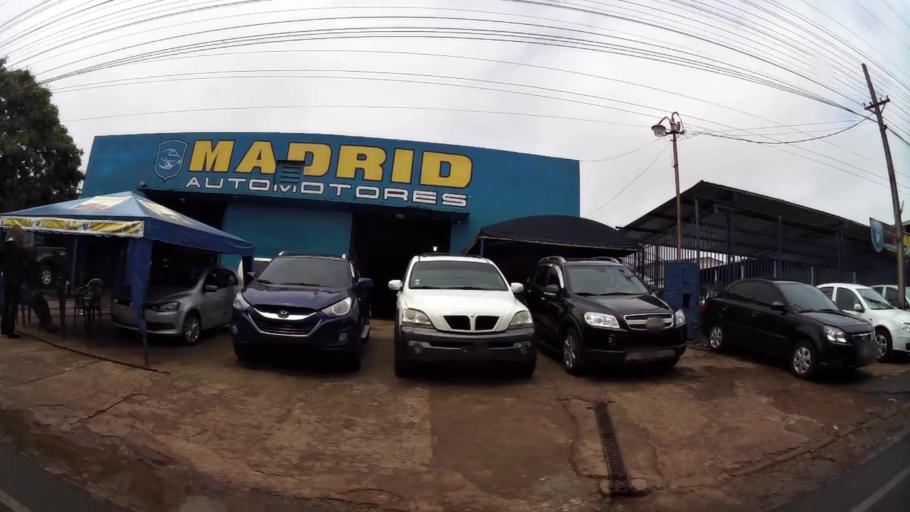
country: PY
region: Alto Parana
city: Ciudad del Este
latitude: -25.5024
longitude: -54.6542
